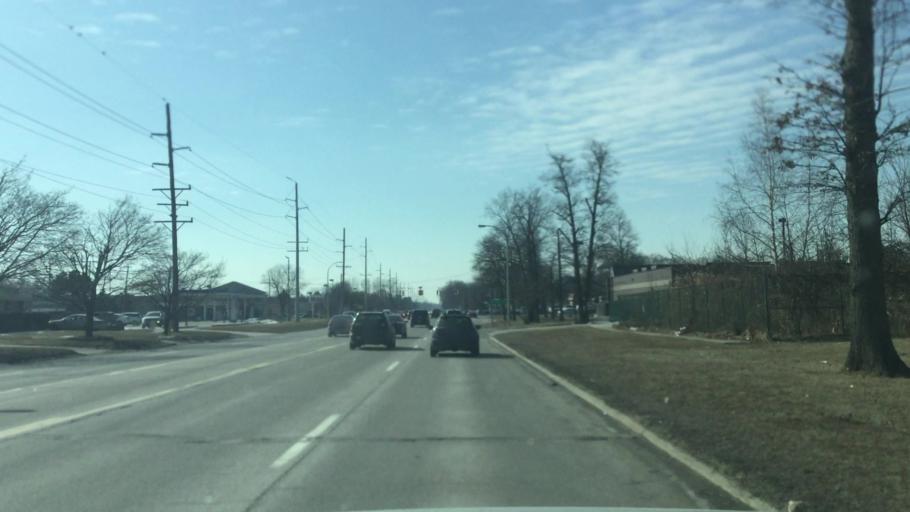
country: US
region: Michigan
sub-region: Wayne County
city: Garden City
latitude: 42.3068
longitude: -83.3468
